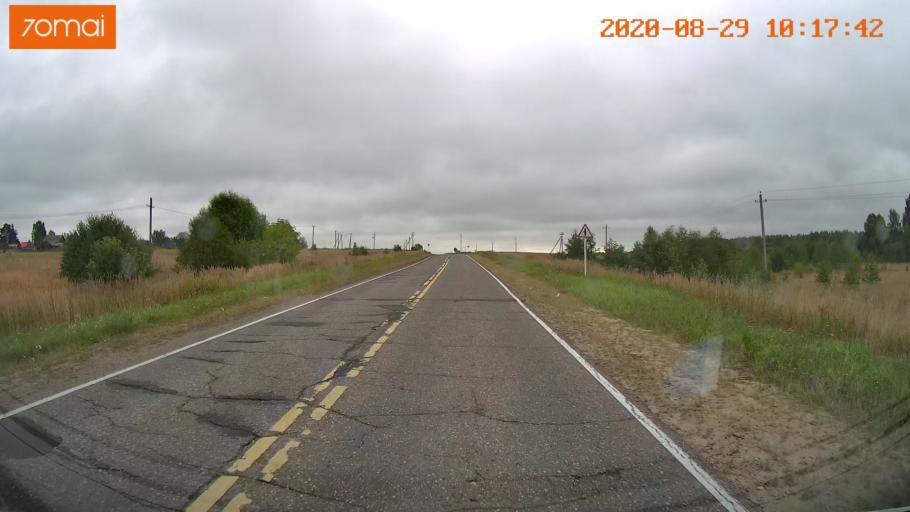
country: RU
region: Ivanovo
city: Yur'yevets
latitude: 57.3334
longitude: 42.8194
